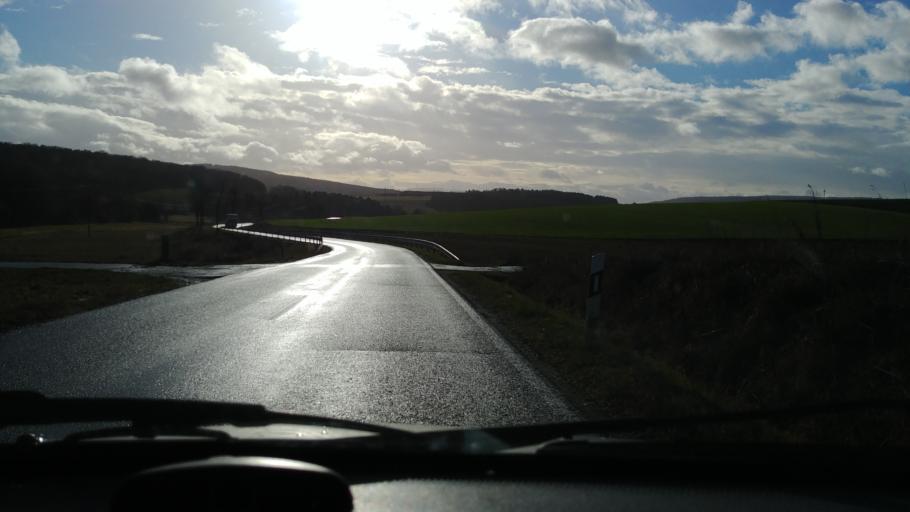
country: DE
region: Hesse
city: Taunusstein
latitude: 50.1765
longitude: 8.1868
